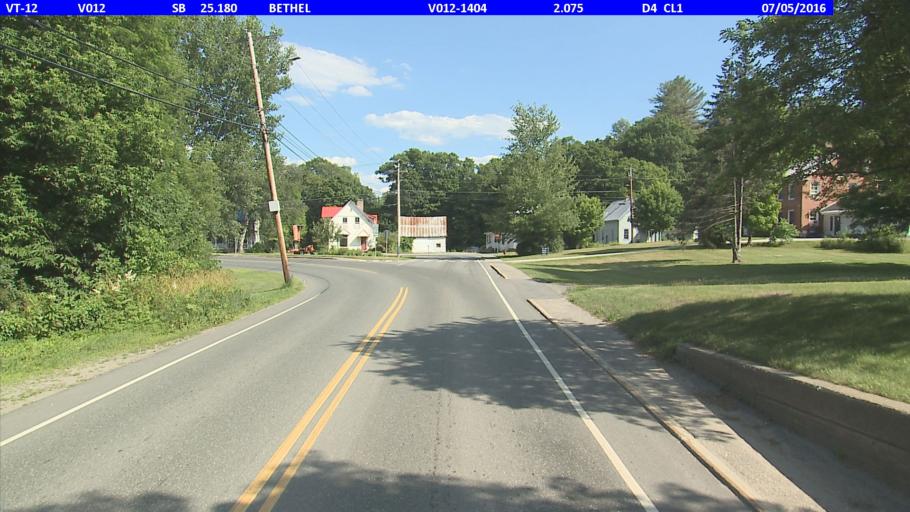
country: US
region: Vermont
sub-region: Orange County
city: Randolph
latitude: 43.8308
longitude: -72.6392
